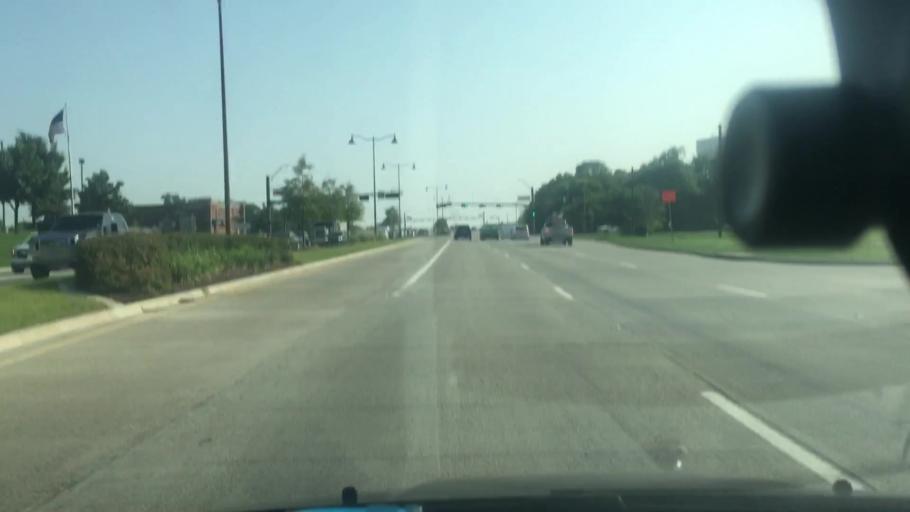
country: US
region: Texas
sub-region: Collin County
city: Prosper
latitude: 33.2372
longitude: -96.7893
